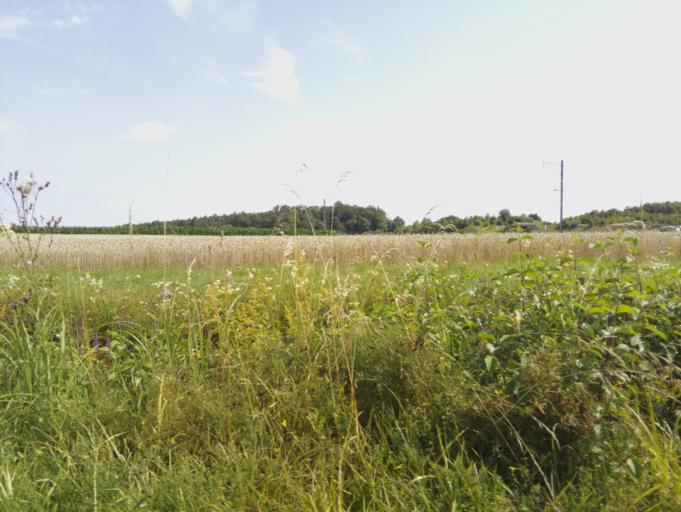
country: CH
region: Zurich
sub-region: Bezirk Andelfingen
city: Henggart
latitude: 47.5754
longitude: 8.6802
